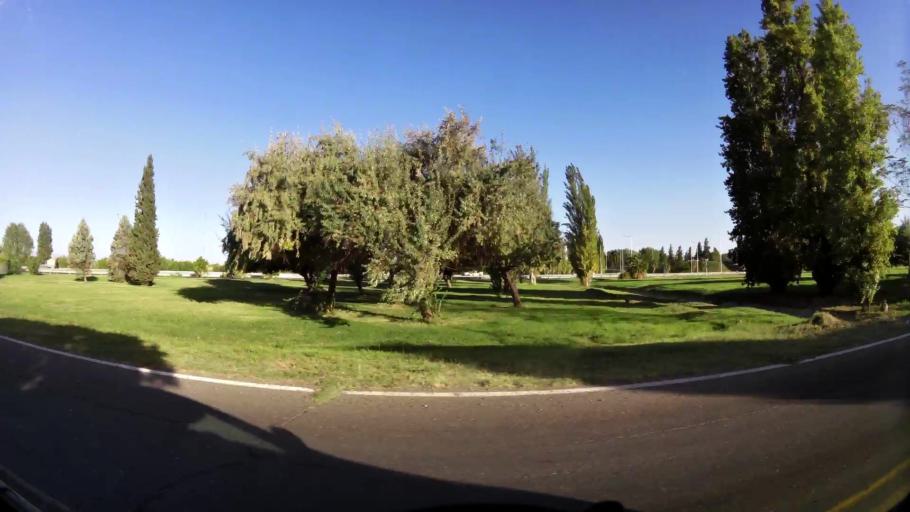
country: AR
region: San Juan
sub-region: Departamento de Santa Lucia
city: Santa Lucia
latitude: -31.5461
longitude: -68.5052
